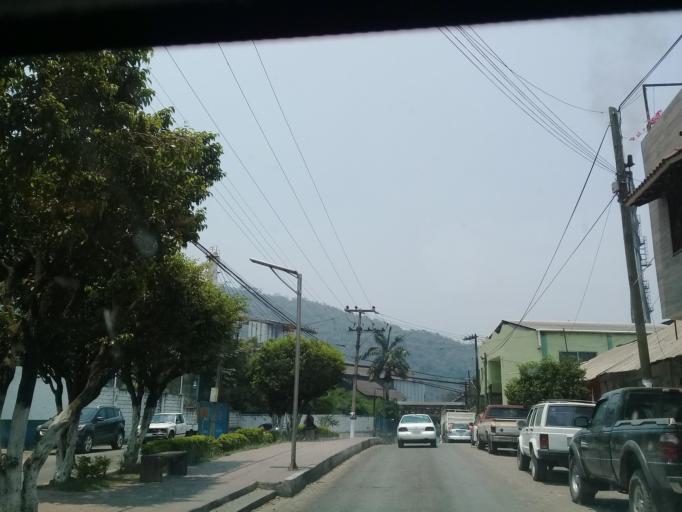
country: MX
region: Veracruz
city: Tezonapa
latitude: 18.6041
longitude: -96.6866
